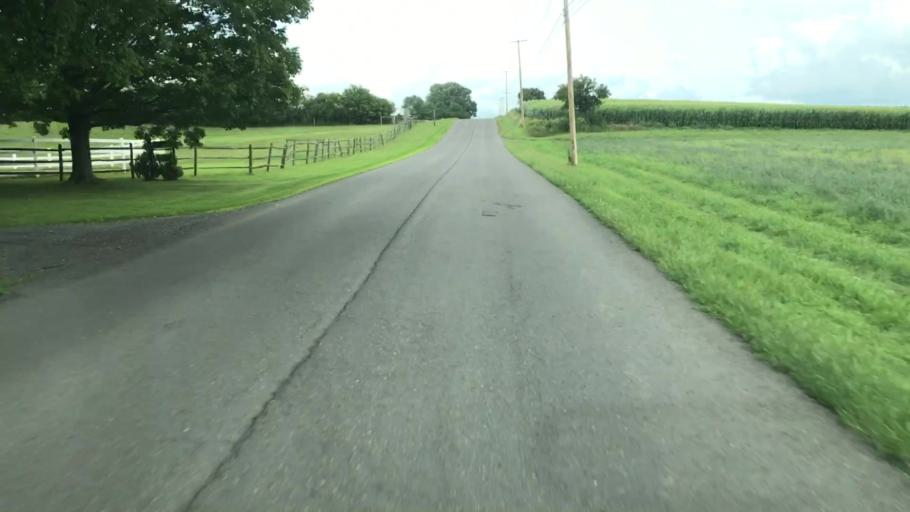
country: US
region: New York
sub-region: Onondaga County
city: Elbridge
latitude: 42.9851
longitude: -76.5016
